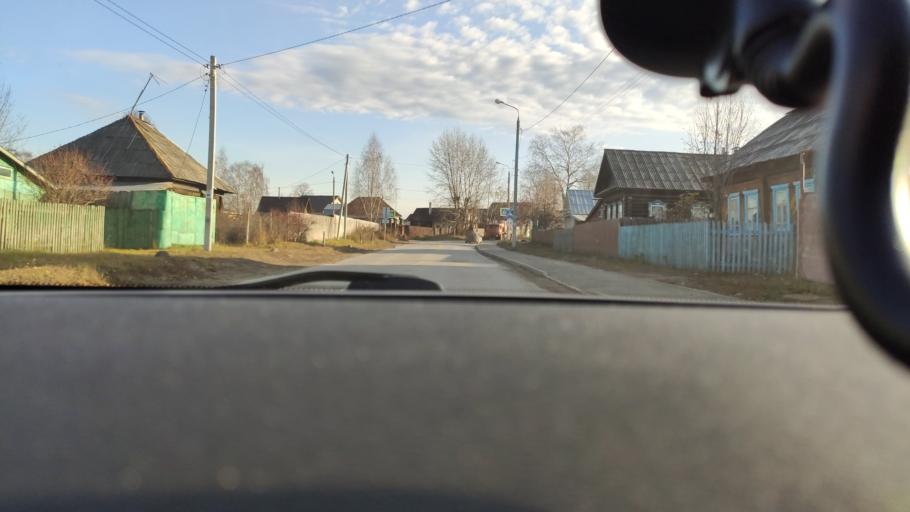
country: RU
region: Perm
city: Kondratovo
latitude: 58.0464
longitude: 56.0415
